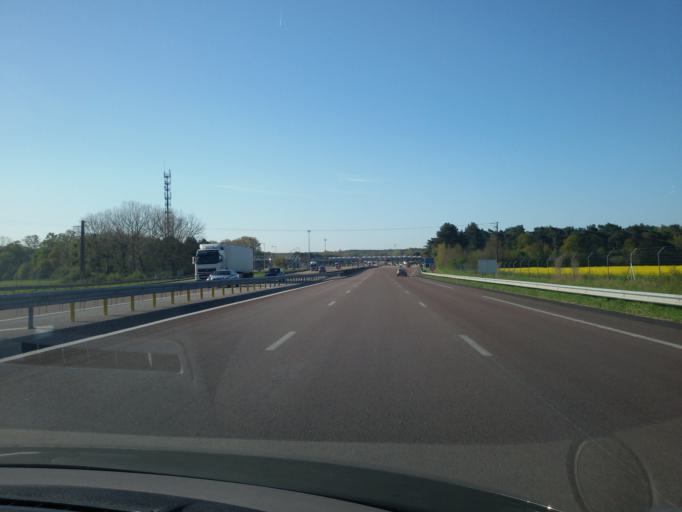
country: FR
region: Ile-de-France
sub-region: Departement de Seine-et-Marne
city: Cely
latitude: 48.4316
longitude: 2.5377
